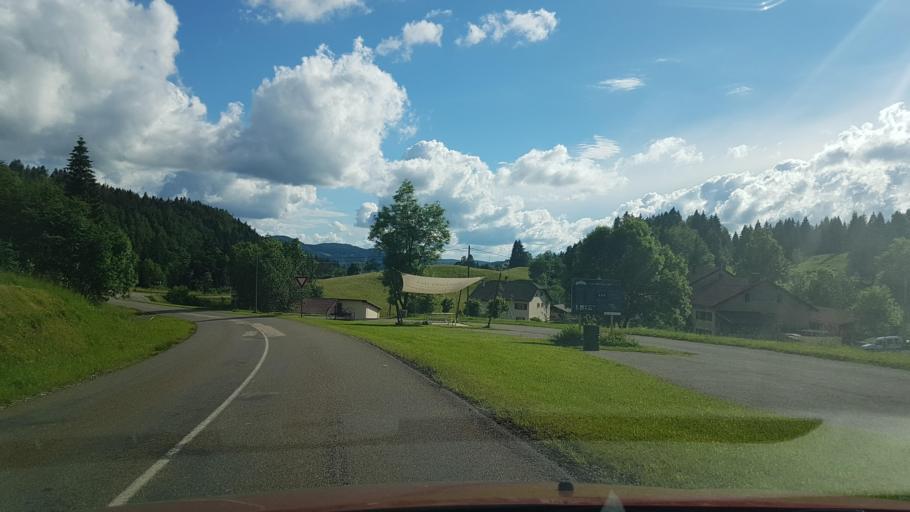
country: FR
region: Franche-Comte
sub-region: Departement du Jura
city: Longchaumois
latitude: 46.3886
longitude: 5.9406
